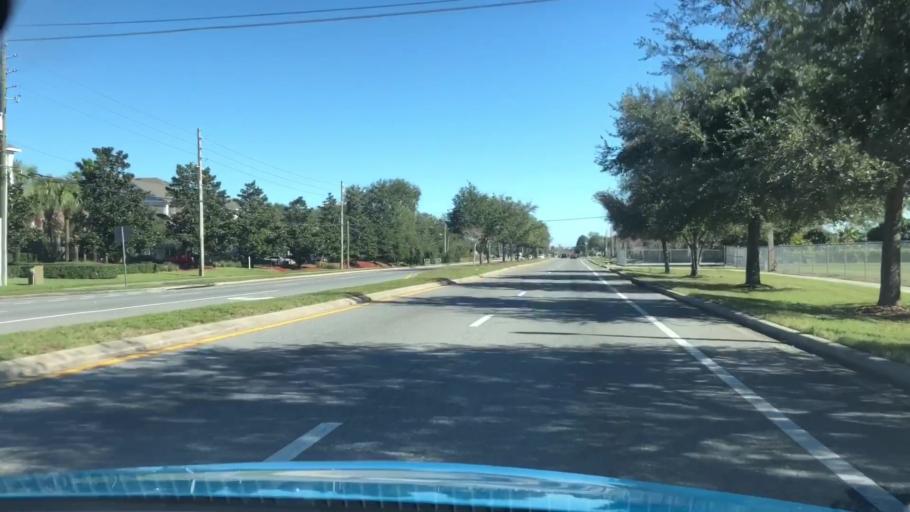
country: US
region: Florida
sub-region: Orange County
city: Oak Ridge
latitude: 28.4868
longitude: -81.4225
